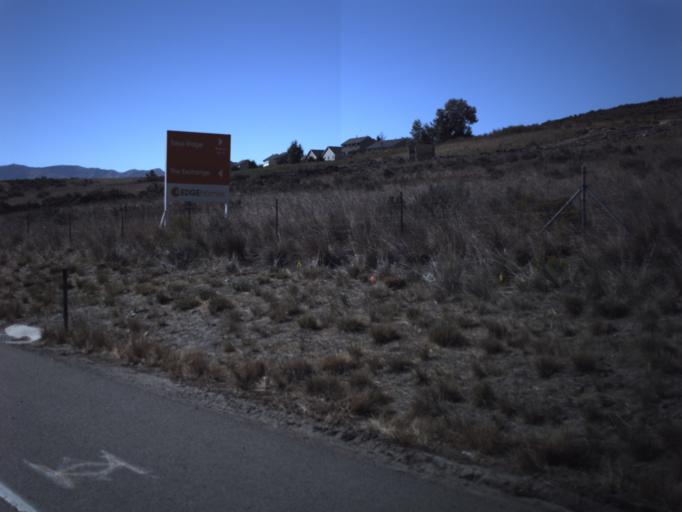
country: US
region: Utah
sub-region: Utah County
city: Saratoga Springs
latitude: 40.4106
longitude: -111.9226
